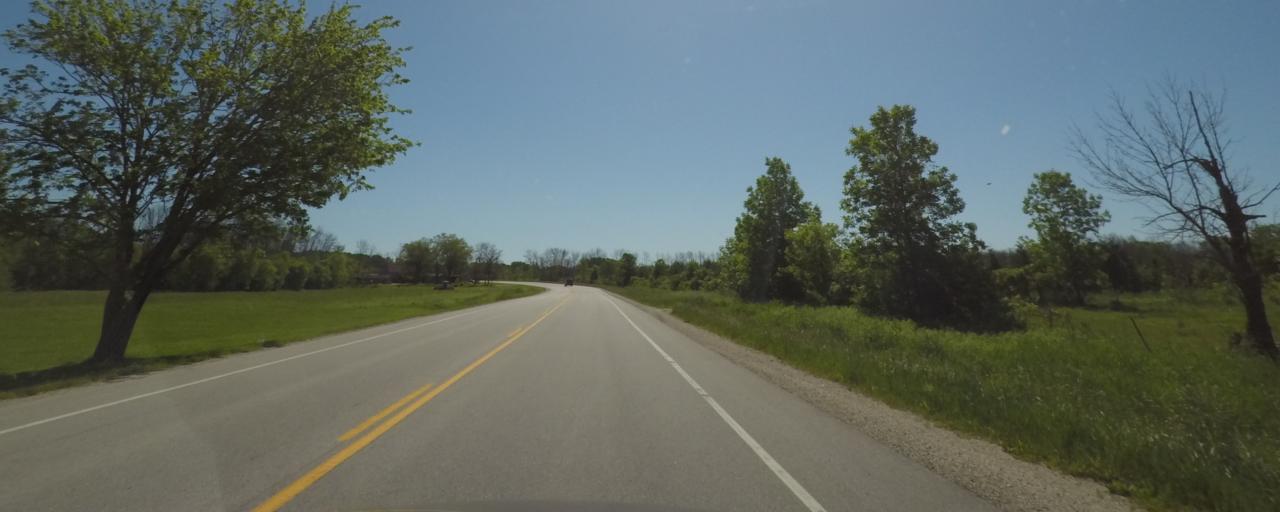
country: US
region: Wisconsin
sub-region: Sheboygan County
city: Plymouth
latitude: 43.7461
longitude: -87.9209
